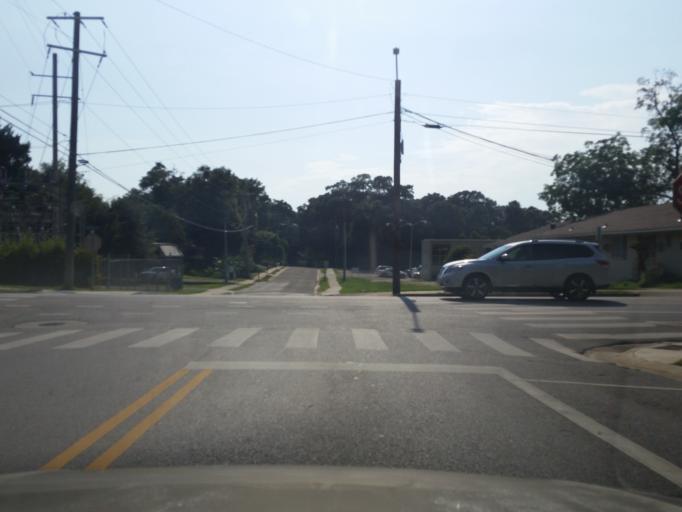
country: US
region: Alabama
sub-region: Baldwin County
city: Fairhope
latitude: 30.5200
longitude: -87.9046
